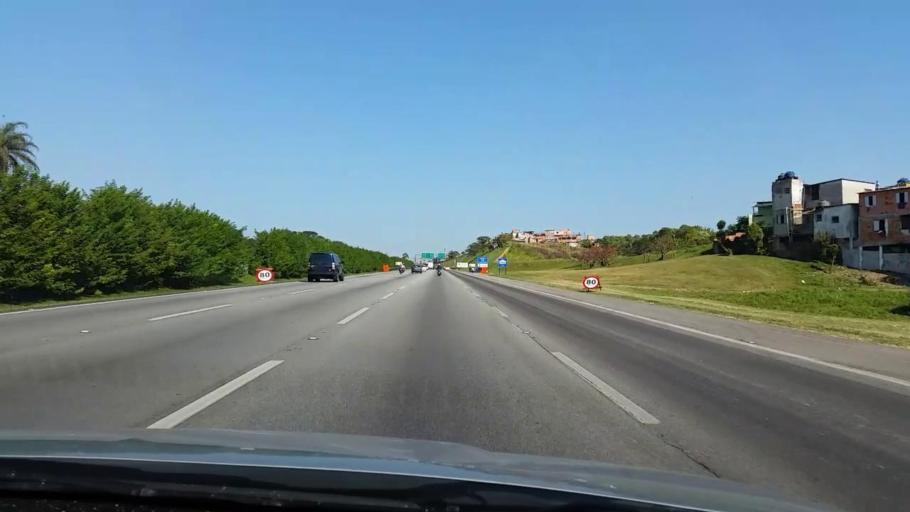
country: BR
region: Sao Paulo
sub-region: Diadema
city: Diadema
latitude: -23.6639
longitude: -46.6333
